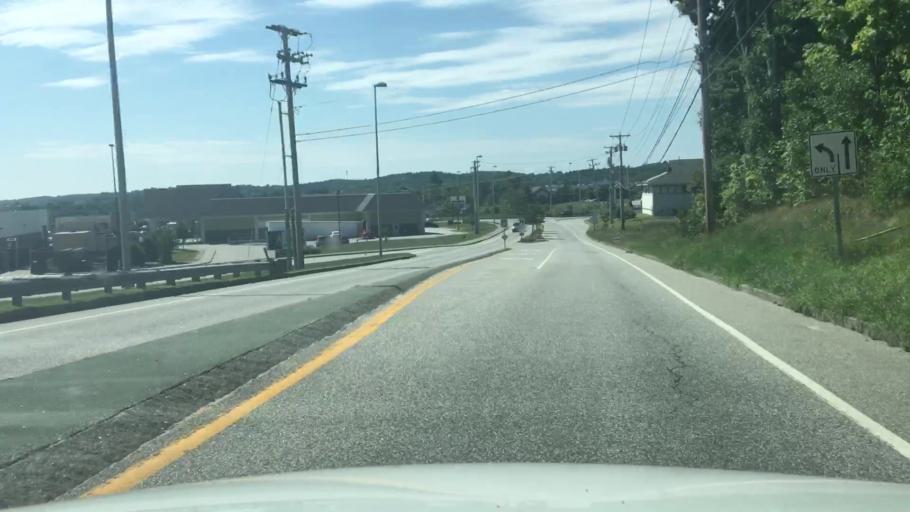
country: US
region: Maine
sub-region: Androscoggin County
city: Auburn
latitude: 44.1236
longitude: -70.2317
